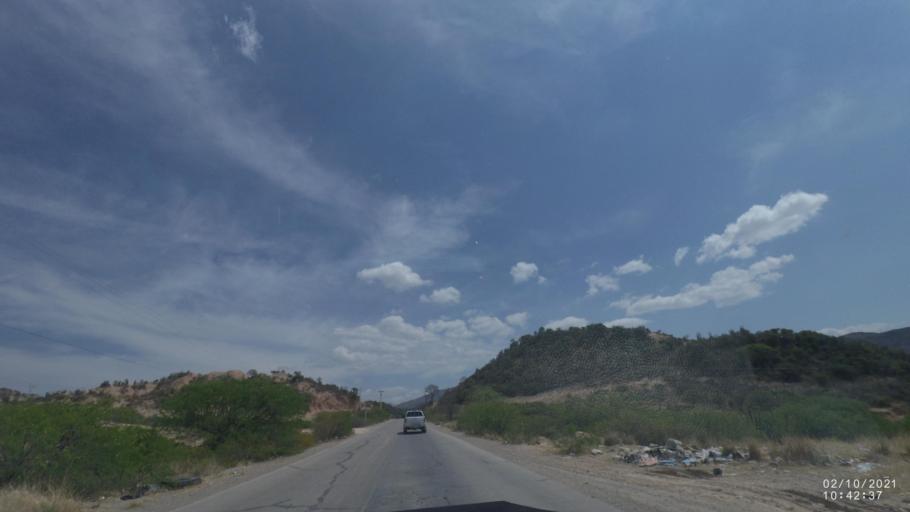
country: BO
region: Cochabamba
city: Capinota
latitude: -17.6056
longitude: -66.2954
